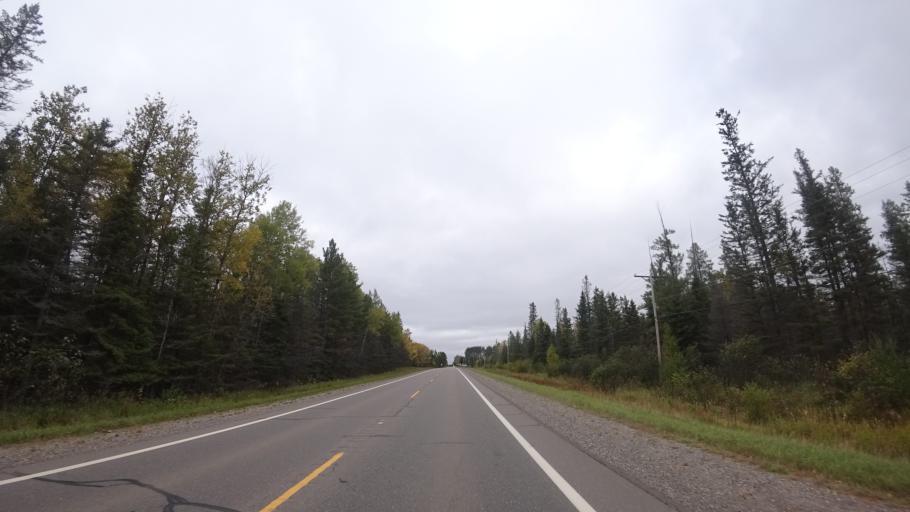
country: US
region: Michigan
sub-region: Iron County
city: Crystal Falls
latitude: 46.1303
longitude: -88.0921
